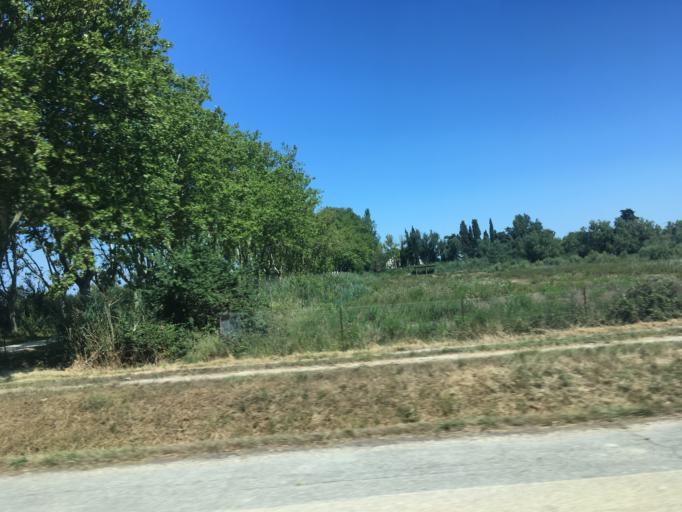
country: FR
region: Languedoc-Roussillon
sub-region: Departement du Gard
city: Saint-Gilles
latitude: 43.6240
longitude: 4.5219
